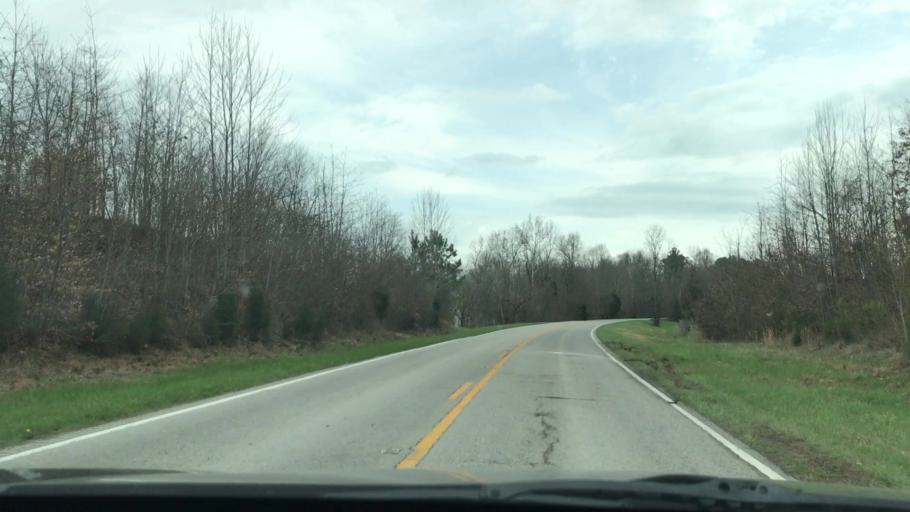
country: US
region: Kentucky
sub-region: Hart County
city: Munfordville
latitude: 37.3148
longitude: -85.7623
